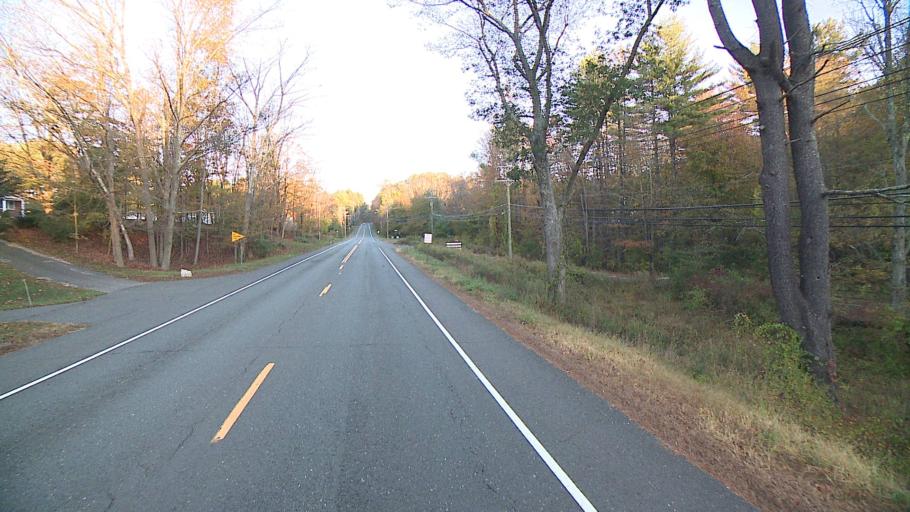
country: US
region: Connecticut
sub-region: Hartford County
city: Collinsville
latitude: 41.8443
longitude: -72.9410
